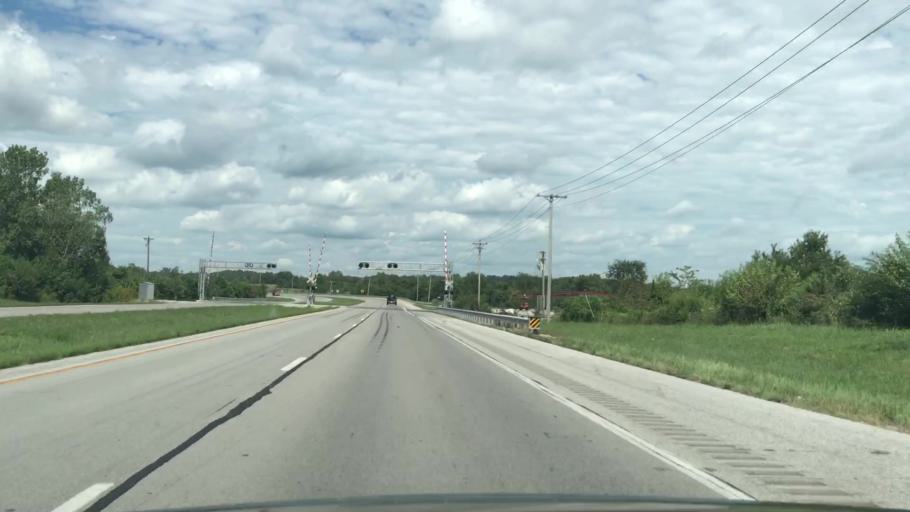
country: US
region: Kentucky
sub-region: Logan County
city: Russellville
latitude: 36.8615
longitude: -86.8635
